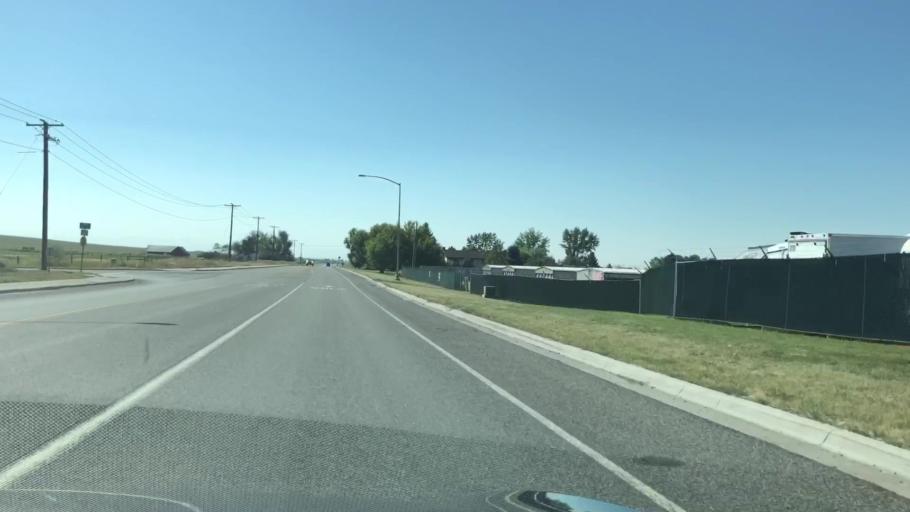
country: US
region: Montana
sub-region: Gallatin County
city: Bozeman
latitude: 45.7292
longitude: -111.0971
